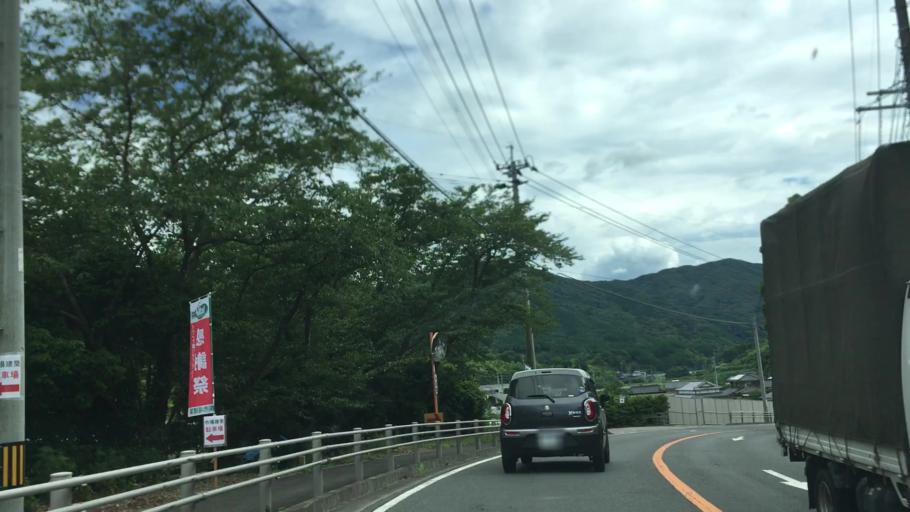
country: JP
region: Nagasaki
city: Sasebo
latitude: 32.9912
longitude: 129.7380
